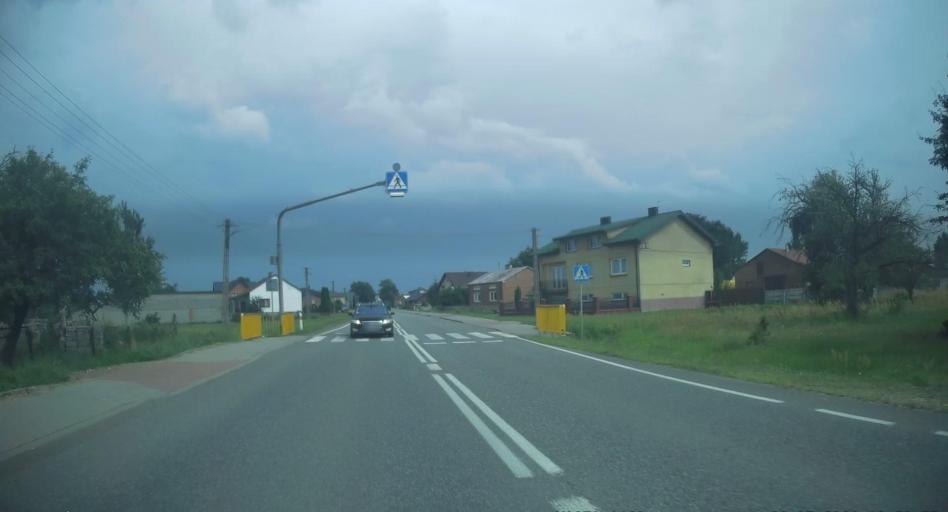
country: PL
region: Lodz Voivodeship
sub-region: Powiat skierniewicki
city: Gluchow
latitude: 51.7727
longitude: 20.1390
